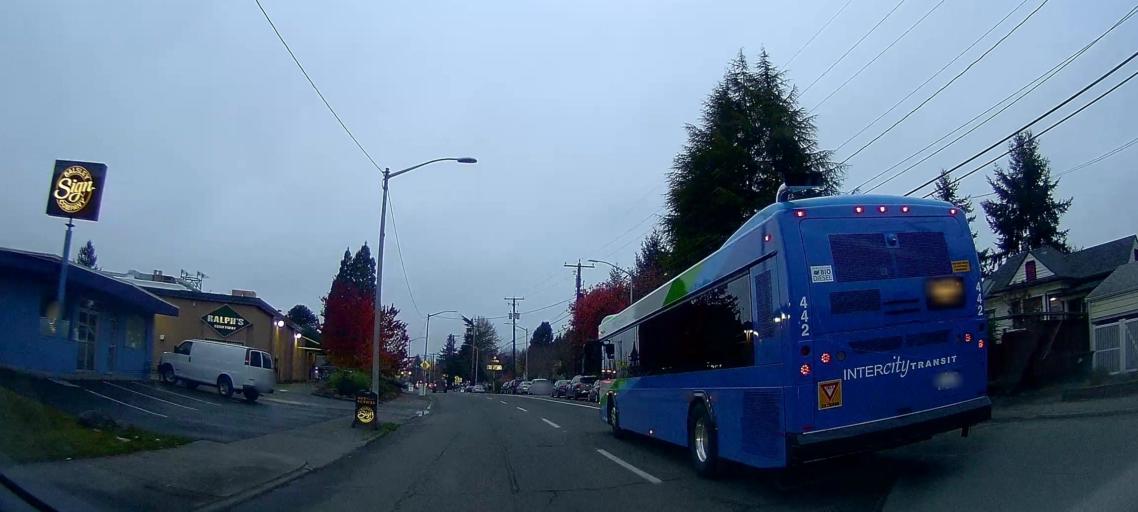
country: US
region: Washington
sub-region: Thurston County
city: Olympia
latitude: 47.0467
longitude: -122.8739
